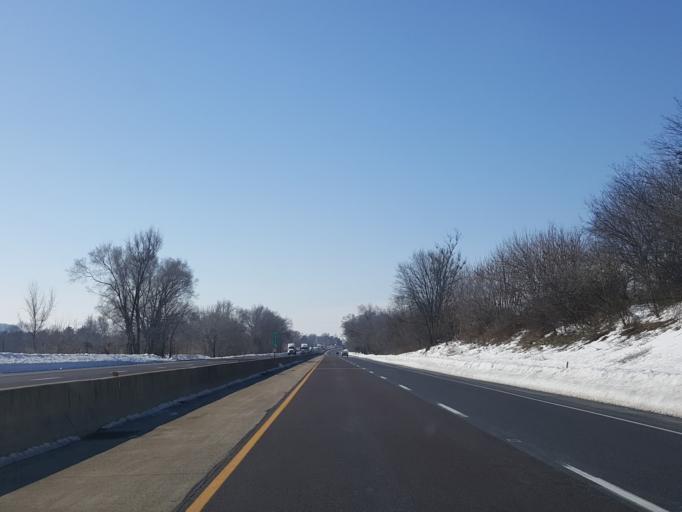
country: US
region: Pennsylvania
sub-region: Lebanon County
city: Myerstown
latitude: 40.4703
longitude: -76.3195
